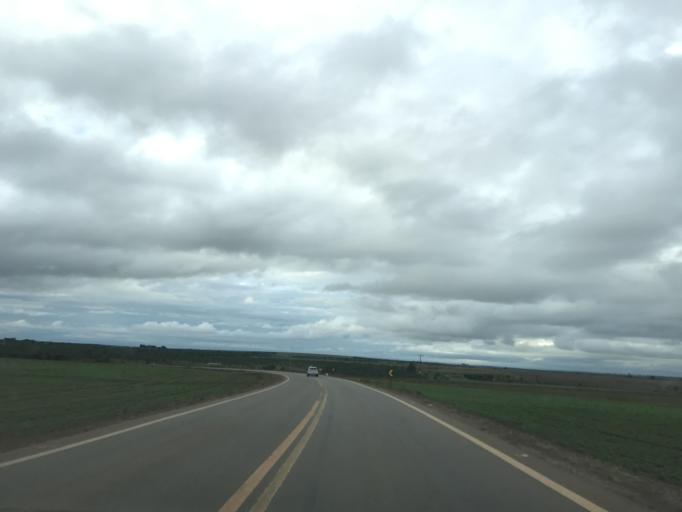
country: BR
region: Goias
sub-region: Luziania
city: Luziania
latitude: -16.4946
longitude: -48.2008
